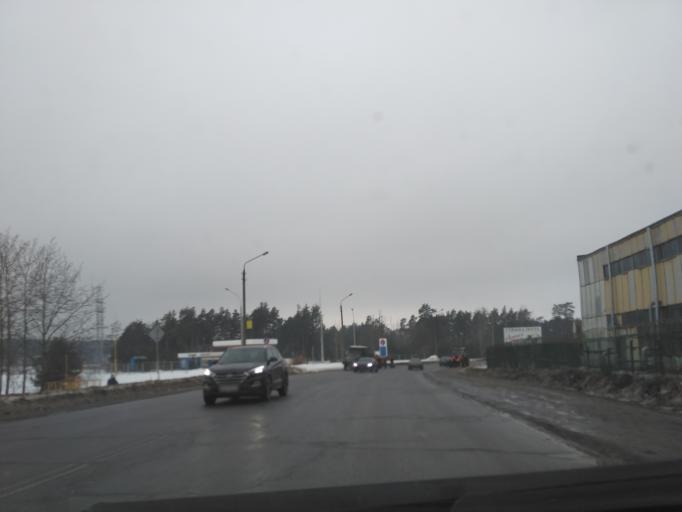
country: BY
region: Minsk
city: Horad Barysaw
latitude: 54.1995
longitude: 28.4873
